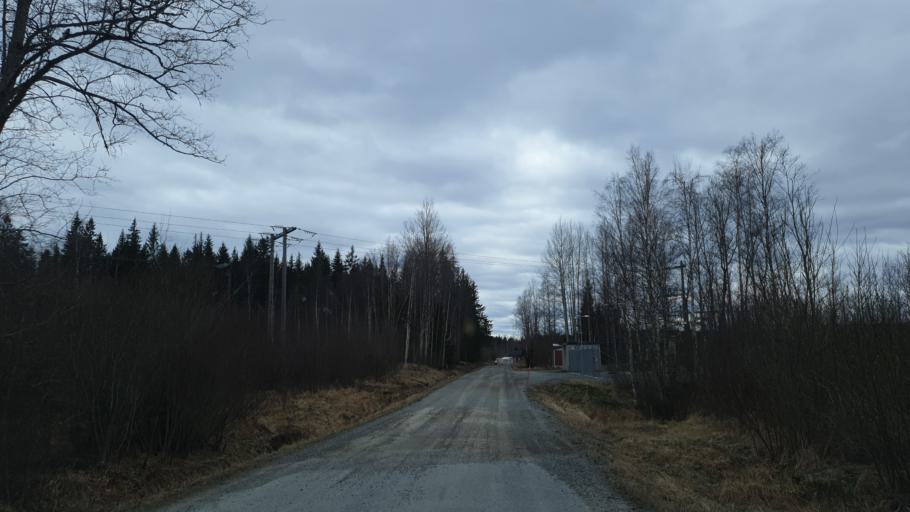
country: SE
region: OErebro
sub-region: Nora Kommun
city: As
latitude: 59.5990
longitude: 14.9182
